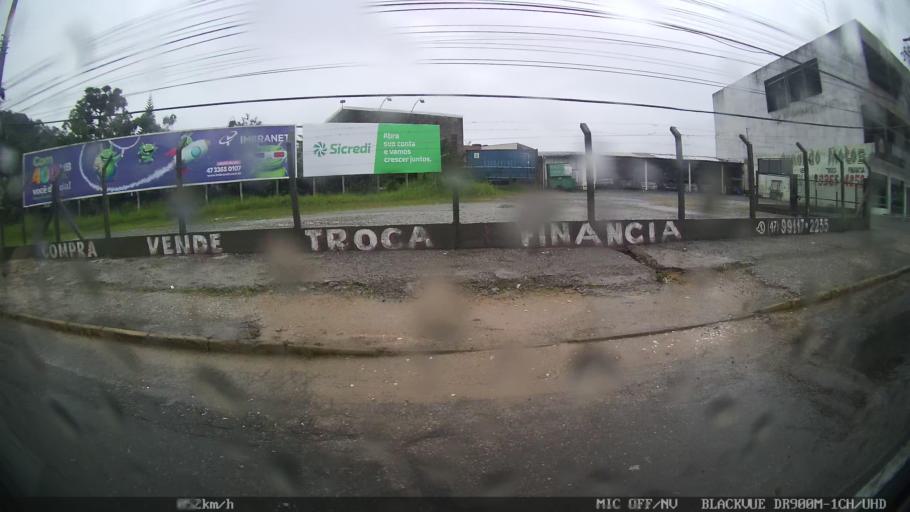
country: BR
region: Santa Catarina
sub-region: Balneario Camboriu
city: Balneario Camboriu
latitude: -27.0149
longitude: -48.6529
